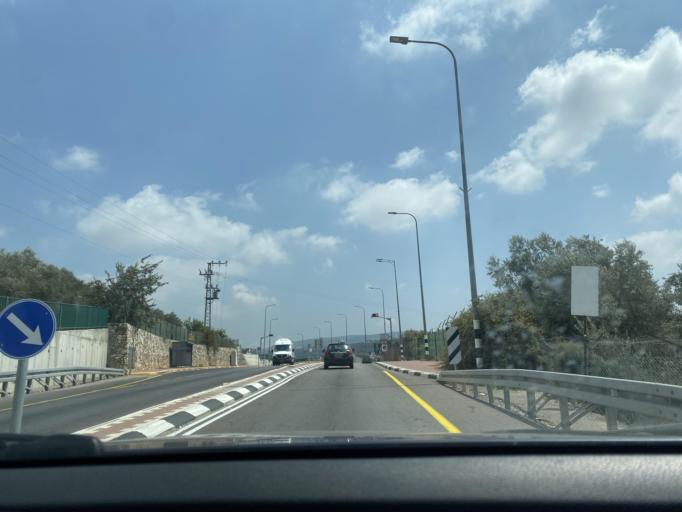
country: IL
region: Northern District
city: Kefar Weradim
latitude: 33.0008
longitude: 35.2989
